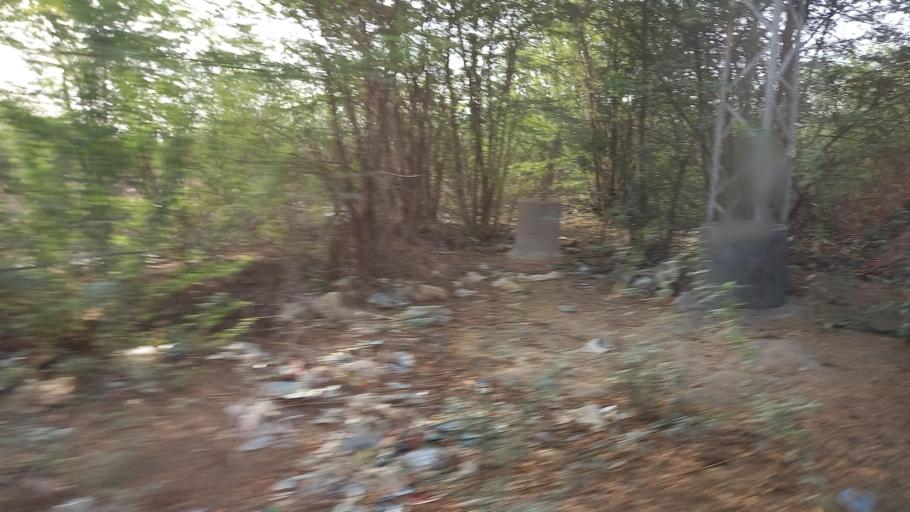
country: PK
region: Sindh
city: Malir Cantonment
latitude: 25.1165
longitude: 67.1916
